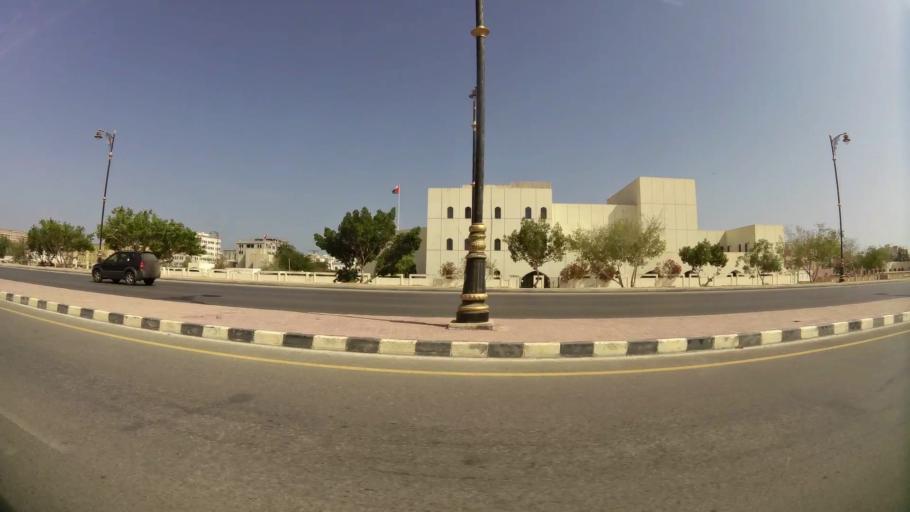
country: OM
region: Zufar
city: Salalah
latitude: 17.0235
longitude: 54.0862
